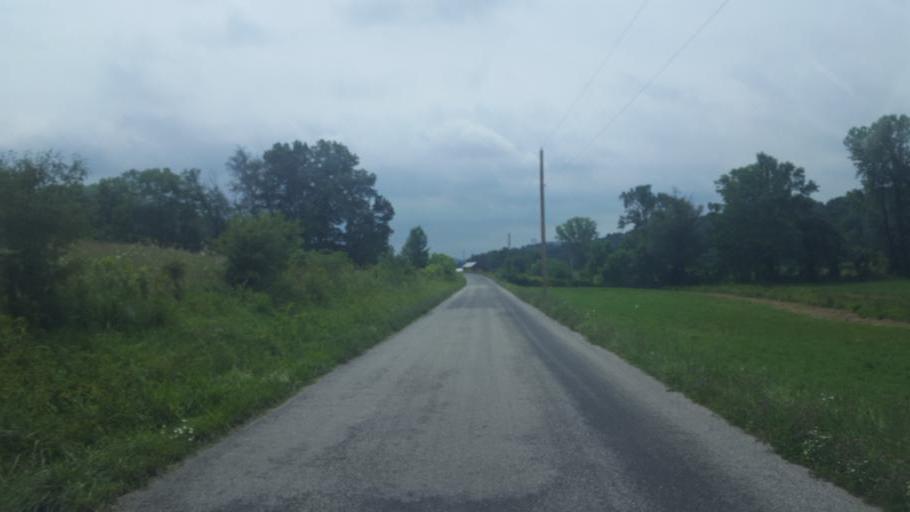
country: US
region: Ohio
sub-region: Licking County
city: Utica
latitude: 40.1745
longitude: -82.4320
